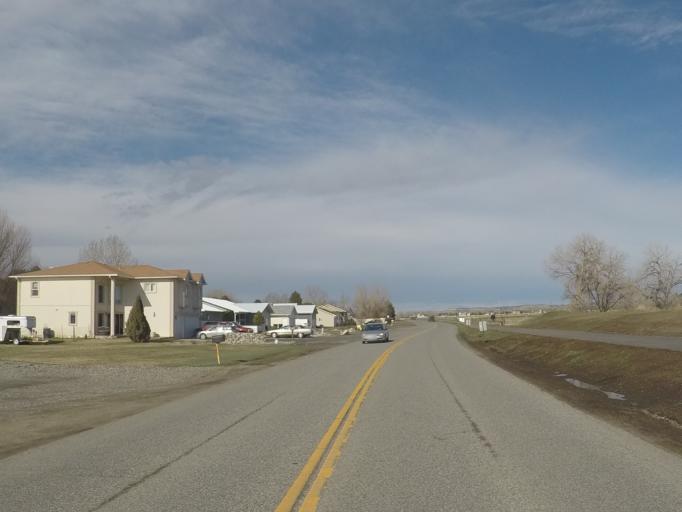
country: US
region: Montana
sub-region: Yellowstone County
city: Billings
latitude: 45.7768
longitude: -108.6082
